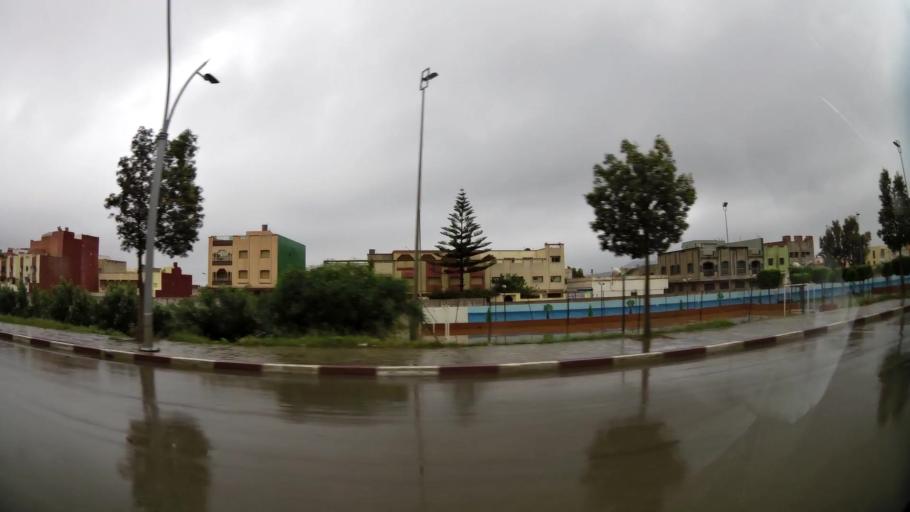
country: MA
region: Oriental
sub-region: Nador
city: Nador
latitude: 35.1593
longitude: -2.9703
